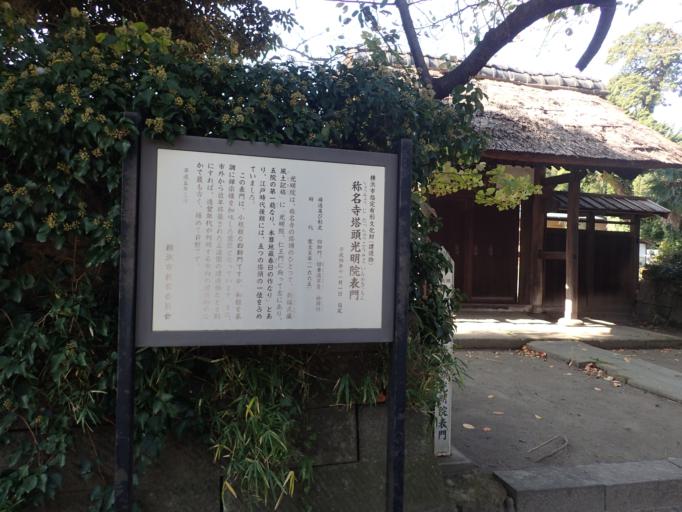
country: JP
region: Kanagawa
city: Yokosuka
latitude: 35.3429
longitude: 139.6298
